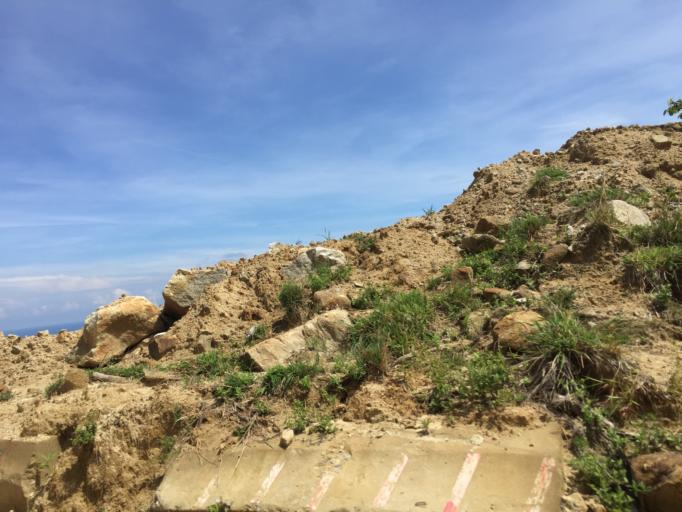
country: VN
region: Quang Nam
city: Hoi An
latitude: 15.9752
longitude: 108.5052
